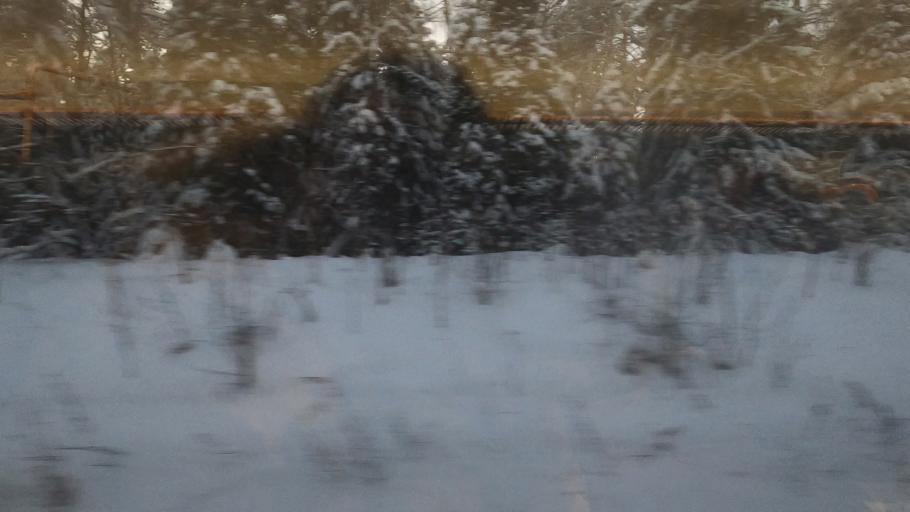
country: RU
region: Moskovskaya
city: Nekrasovskiy
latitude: 56.1132
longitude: 37.5116
